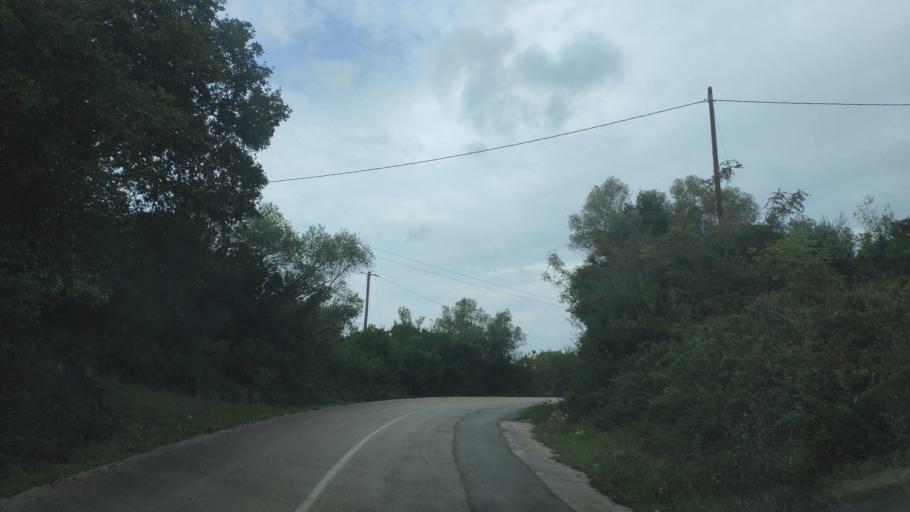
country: GR
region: West Greece
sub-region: Nomos Aitolias kai Akarnanias
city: Vonitsa
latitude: 38.9206
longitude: 20.8588
